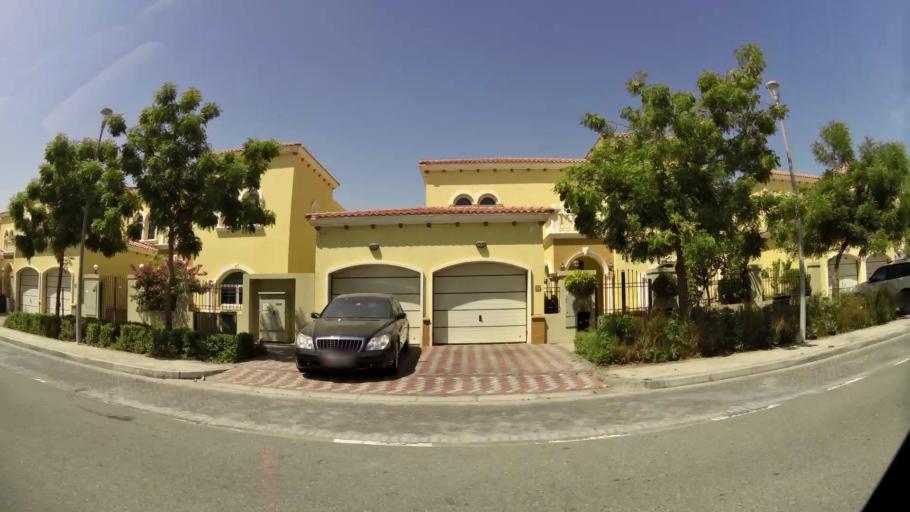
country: AE
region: Dubai
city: Dubai
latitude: 25.0515
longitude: 55.1505
